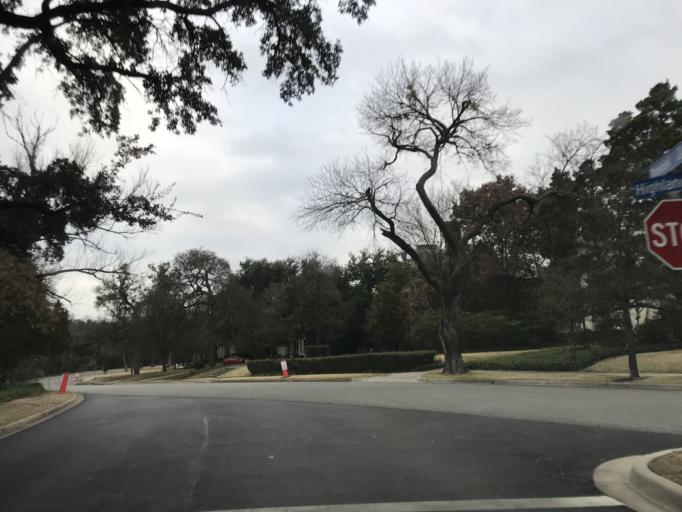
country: US
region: Texas
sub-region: Dallas County
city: Highland Park
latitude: 32.8259
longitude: -96.7985
